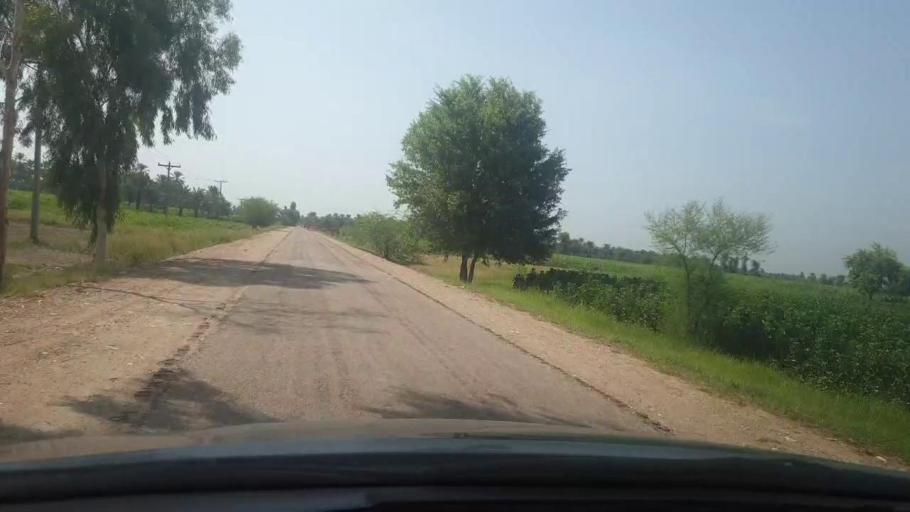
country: PK
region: Sindh
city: Ranipur
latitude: 27.2898
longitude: 68.5763
